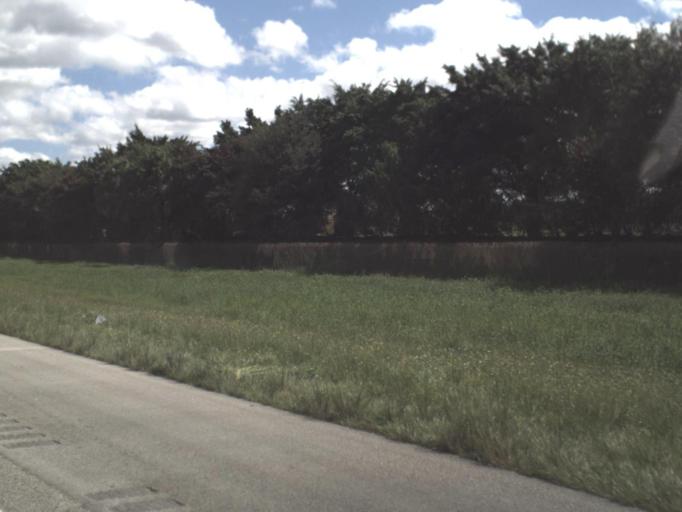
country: US
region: Florida
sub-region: Miami-Dade County
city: Country Club
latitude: 25.9699
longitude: -80.3231
